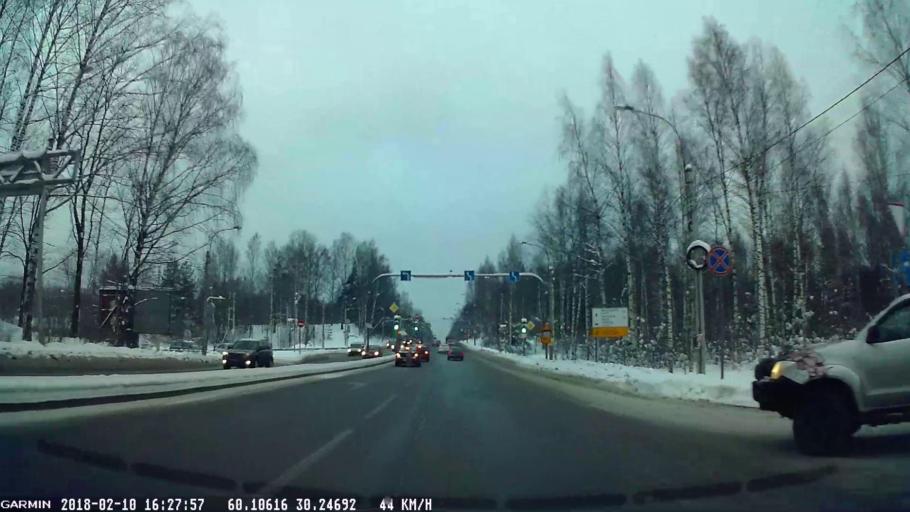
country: RU
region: St.-Petersburg
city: Pargolovo
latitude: 60.1064
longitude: 30.2467
